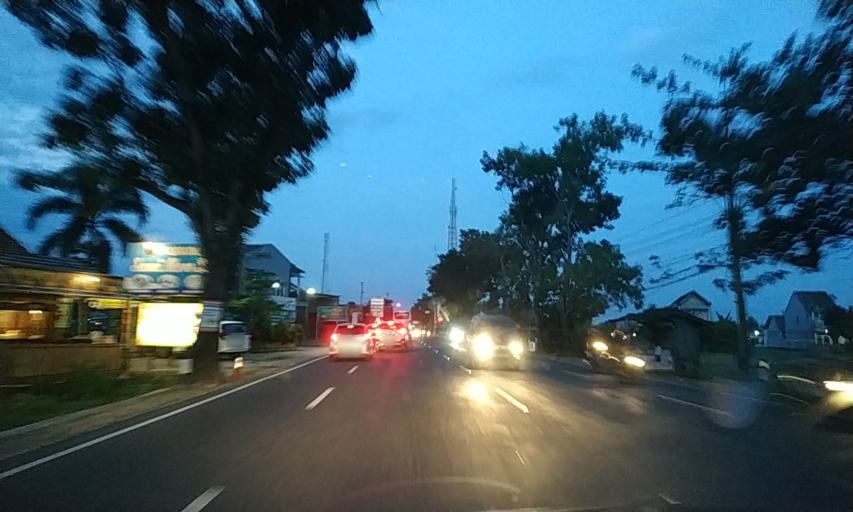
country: ID
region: Daerah Istimewa Yogyakarta
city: Godean
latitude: -7.8145
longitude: 110.2555
